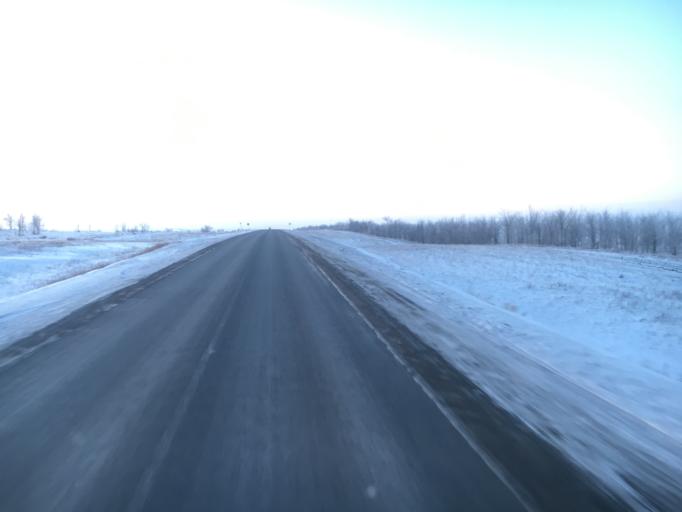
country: KZ
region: Aqtoebe
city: Aqtobe
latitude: 50.2845
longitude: 57.7327
